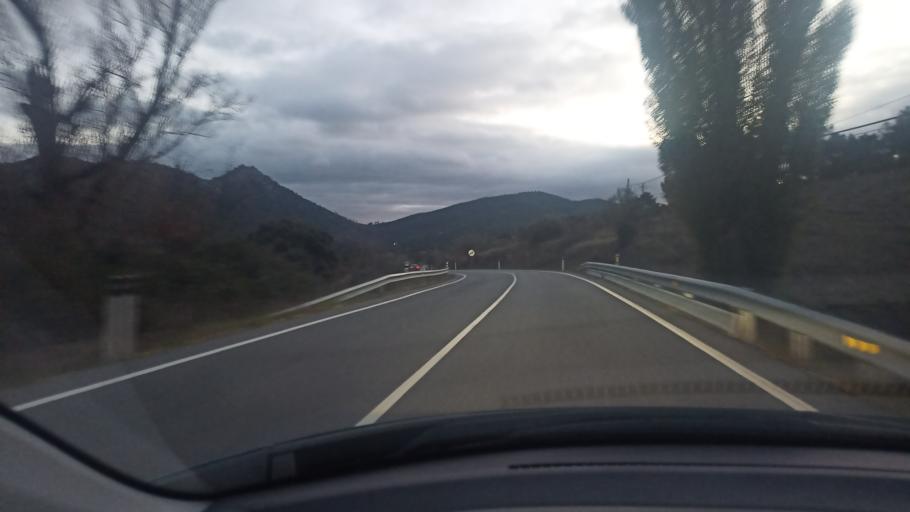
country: ES
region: Madrid
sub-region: Provincia de Madrid
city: Robledo de Chavela
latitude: 40.4813
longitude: -4.2545
